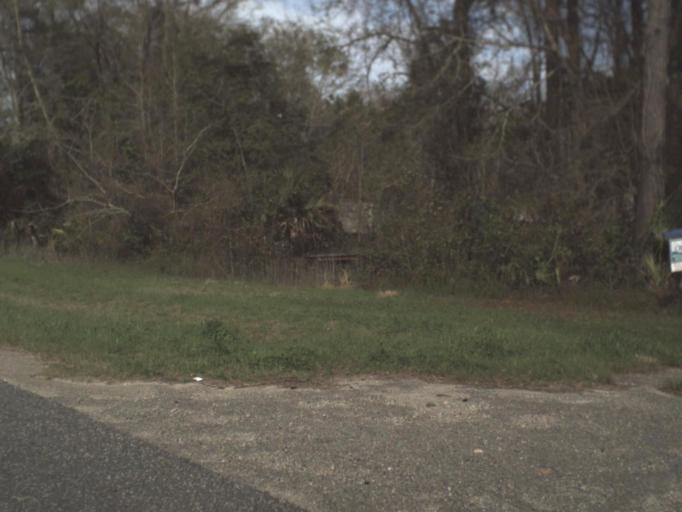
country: US
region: Florida
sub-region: Jefferson County
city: Monticello
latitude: 30.5165
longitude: -83.8747
